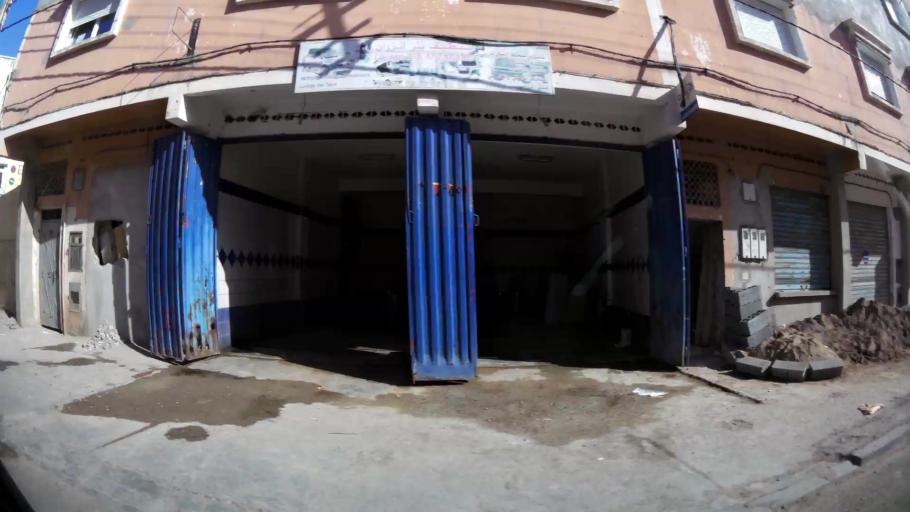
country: MA
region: Souss-Massa-Draa
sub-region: Inezgane-Ait Mellou
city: Inezgane
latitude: 30.3759
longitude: -9.5090
